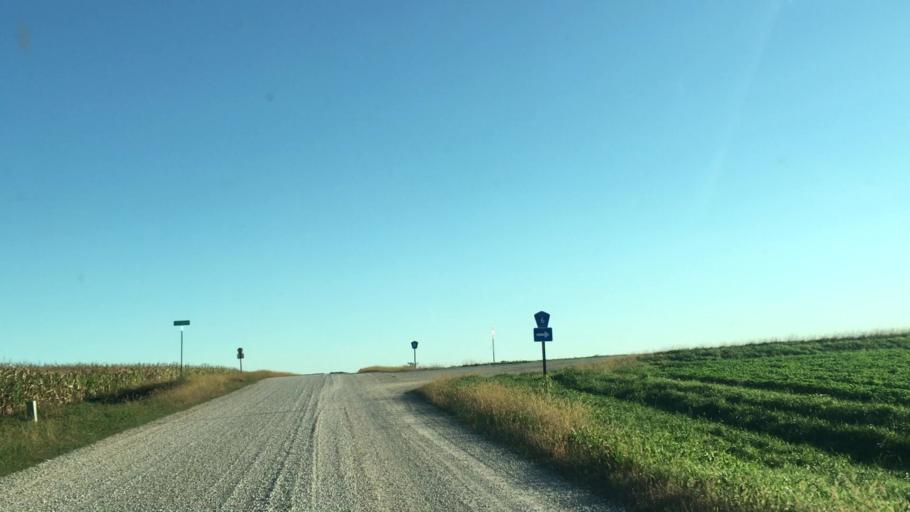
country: US
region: Minnesota
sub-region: Fillmore County
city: Preston
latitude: 43.7716
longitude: -92.0294
